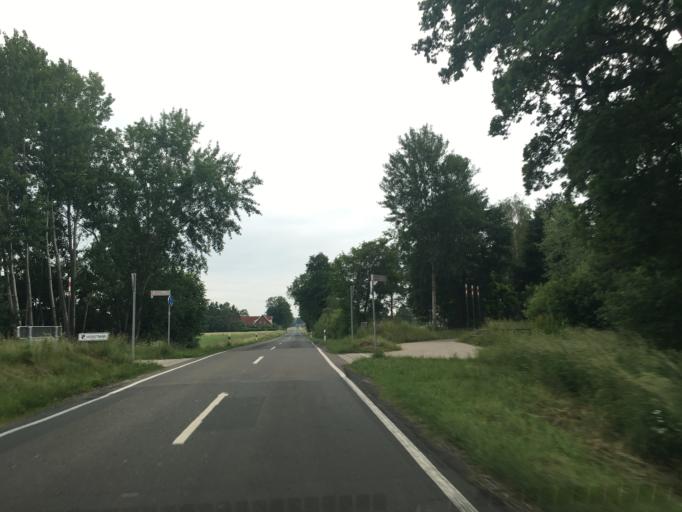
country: DE
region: North Rhine-Westphalia
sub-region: Regierungsbezirk Munster
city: Steinfurt
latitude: 52.1130
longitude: 7.3369
